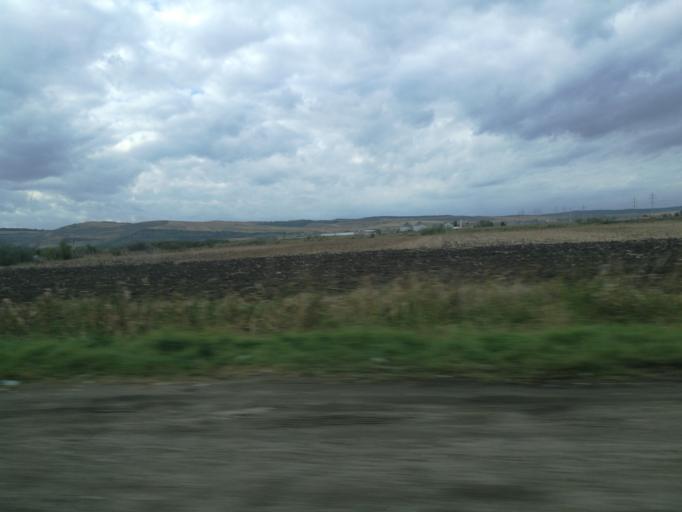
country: RO
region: Mures
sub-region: Comuna Cristesti
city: Cristesti
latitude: 46.4941
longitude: 24.4751
